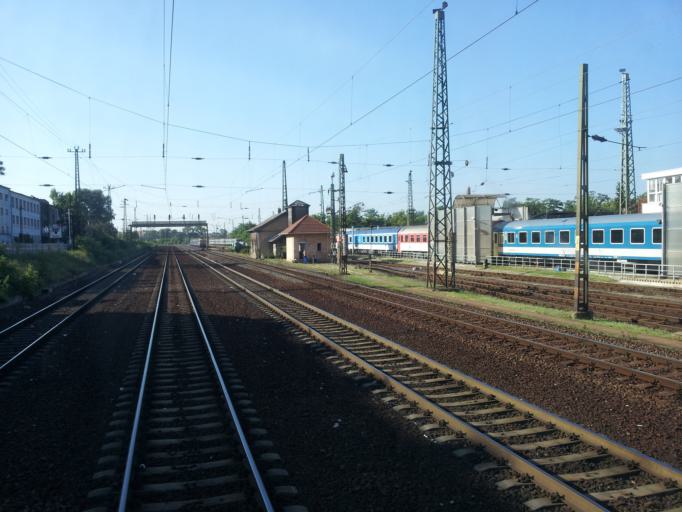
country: HU
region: Budapest
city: Budapest XIV. keruelet
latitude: 47.4955
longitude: 19.1006
